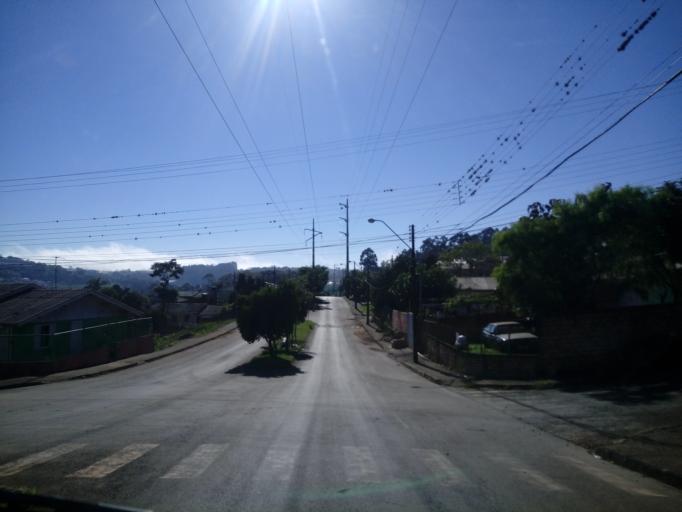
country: BR
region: Santa Catarina
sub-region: Chapeco
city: Chapeco
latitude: -27.0666
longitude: -52.6047
